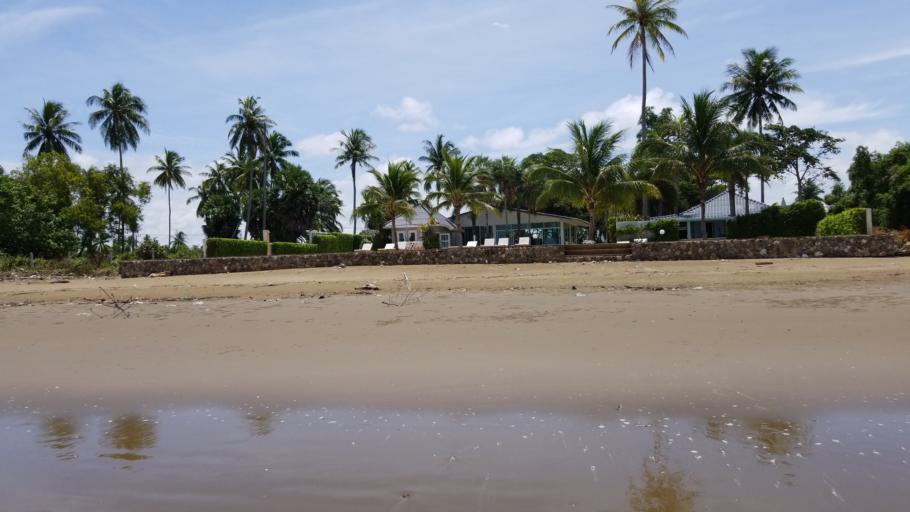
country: TH
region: Krabi
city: Nuea Khlong
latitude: 7.9472
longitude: 98.9655
